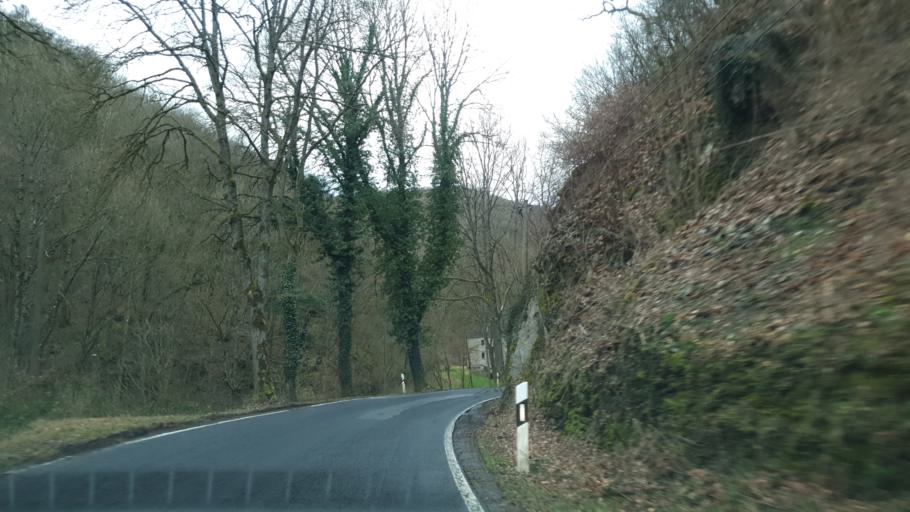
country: DE
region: Rheinland-Pfalz
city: Biebrich
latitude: 50.3187
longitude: 7.9384
